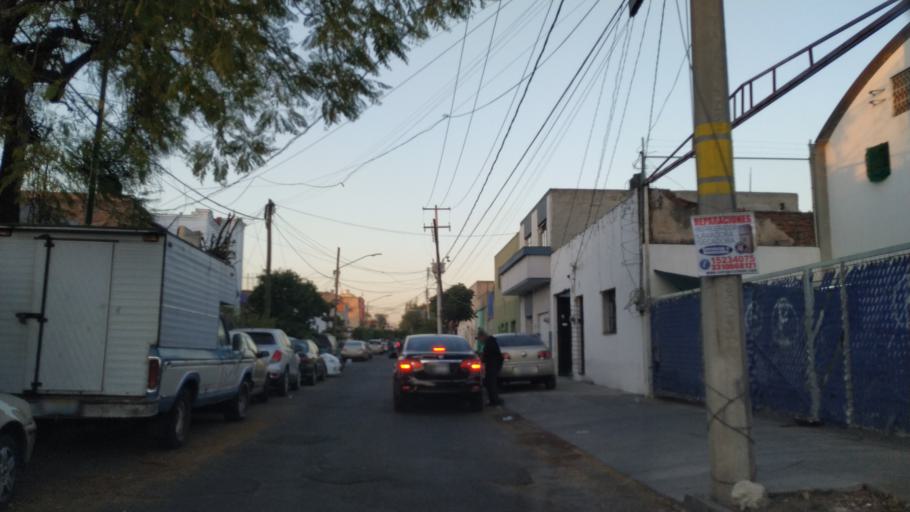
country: MX
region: Jalisco
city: Tlaquepaque
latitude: 20.6517
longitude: -103.3321
